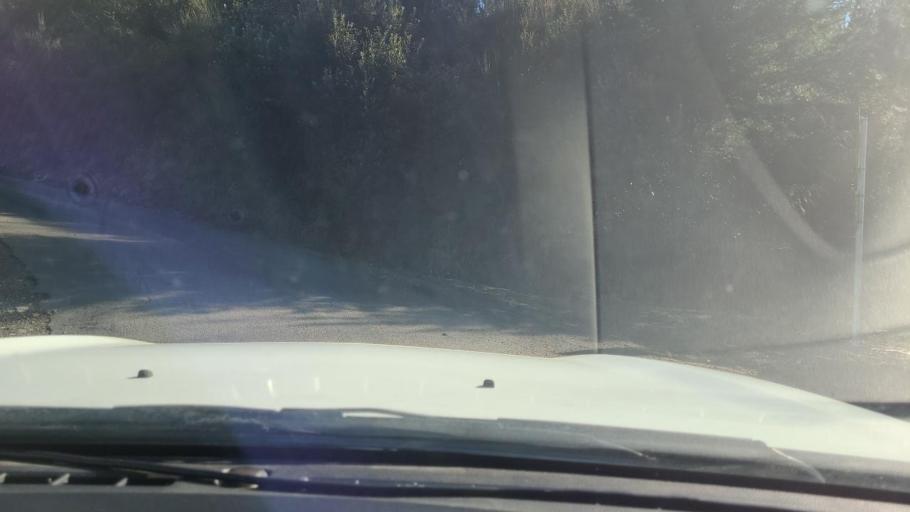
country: NZ
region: Hawke's Bay
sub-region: Napier City
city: Taradale
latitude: -39.1990
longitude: 176.5106
